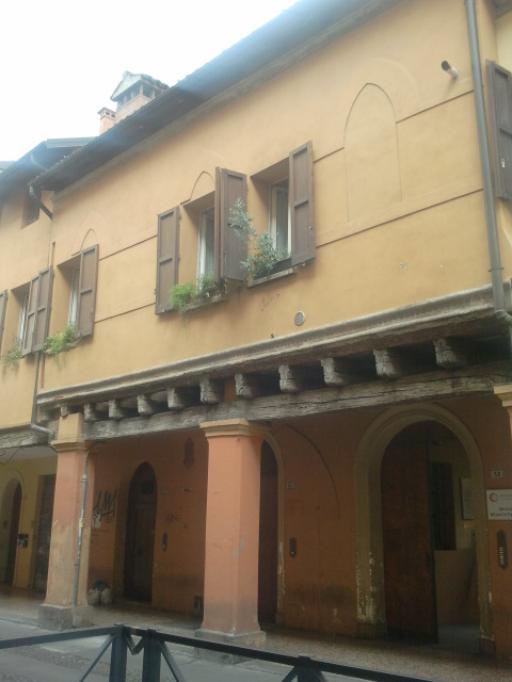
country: IT
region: Emilia-Romagna
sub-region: Provincia di Bologna
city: Bologna
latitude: 44.4955
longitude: 11.3323
